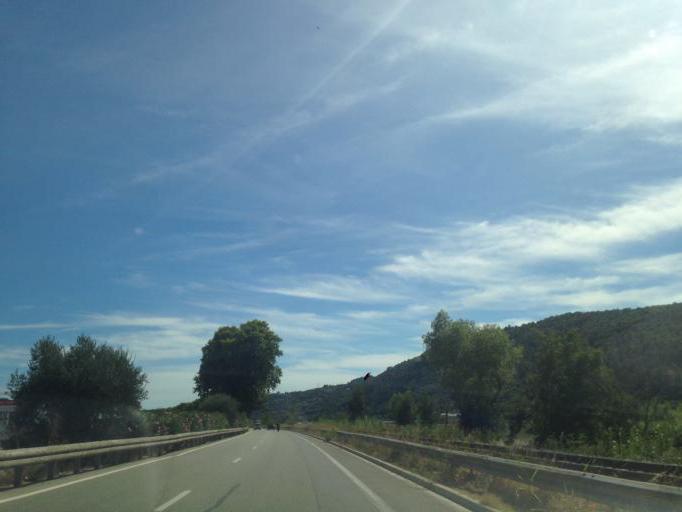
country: FR
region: Provence-Alpes-Cote d'Azur
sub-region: Departement des Alpes-Maritimes
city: Gattieres
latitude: 43.7429
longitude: 7.1853
